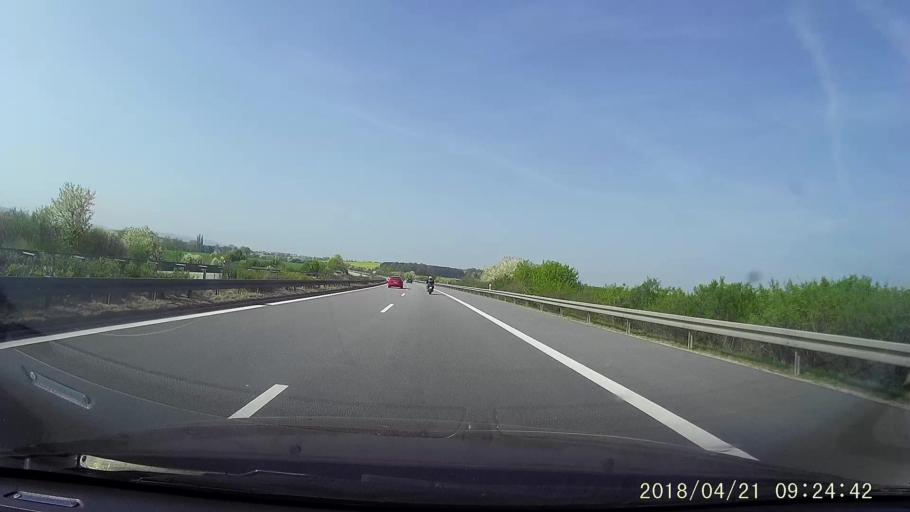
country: DE
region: Saxony
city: Malschwitz
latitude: 51.2070
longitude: 14.4920
